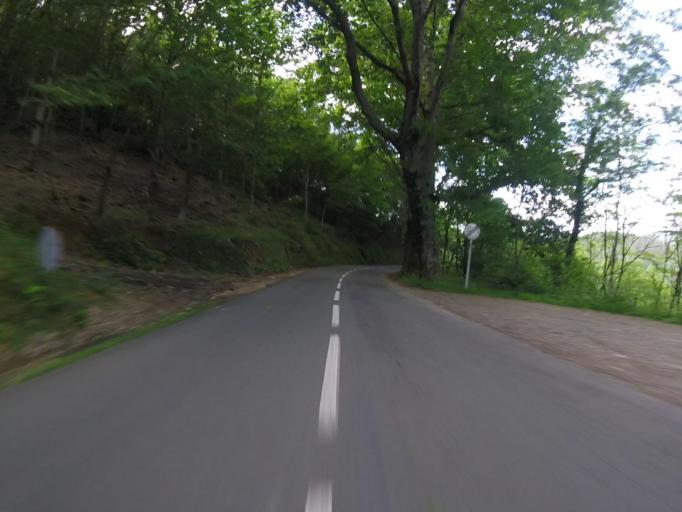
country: ES
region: Basque Country
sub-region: Provincia de Guipuzcoa
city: Errenteria
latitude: 43.2726
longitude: -1.8452
